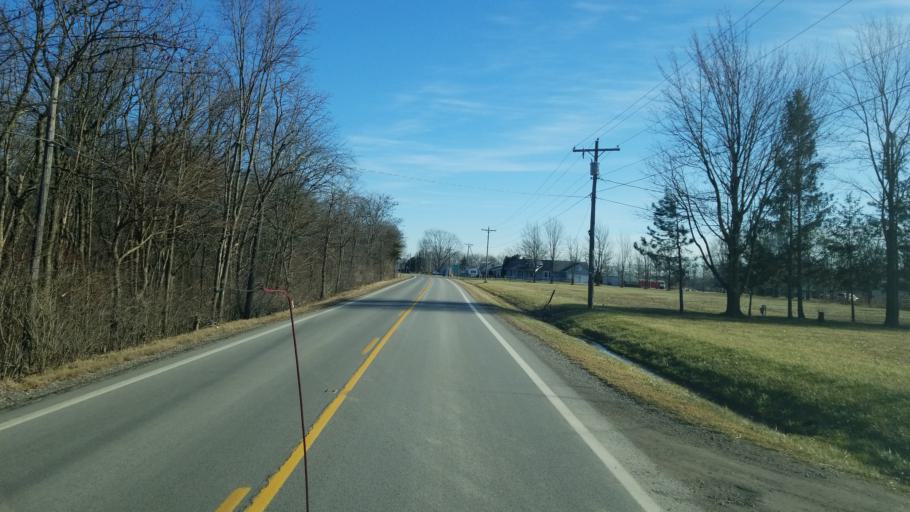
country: US
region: Ohio
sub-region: Wood County
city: Weston
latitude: 41.4102
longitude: -83.8852
